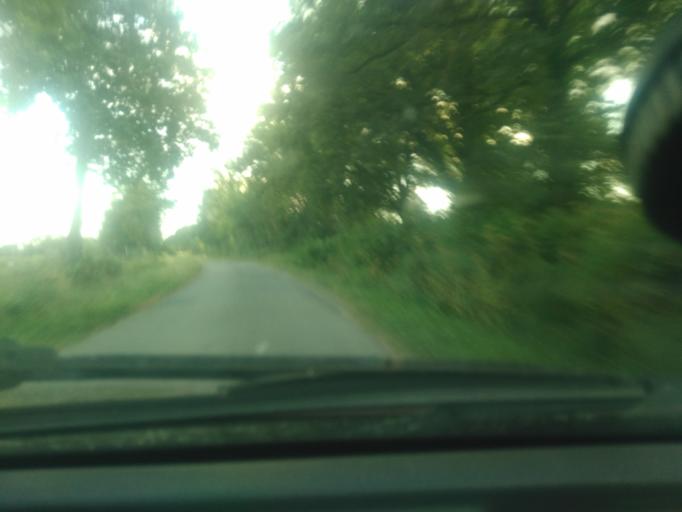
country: FR
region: Pays de la Loire
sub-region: Departement de la Vendee
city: La Ferriere
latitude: 46.7104
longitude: -1.3006
